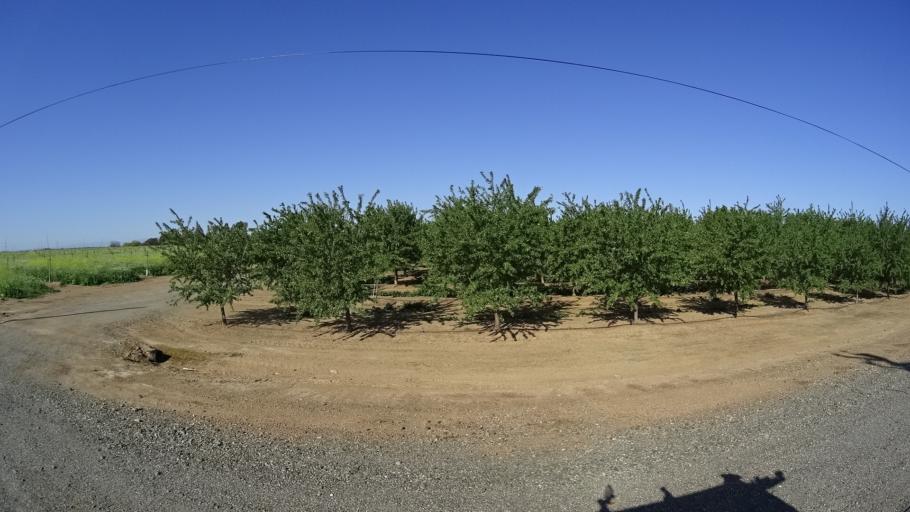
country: US
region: California
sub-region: Glenn County
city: Hamilton City
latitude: 39.7795
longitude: -122.0853
